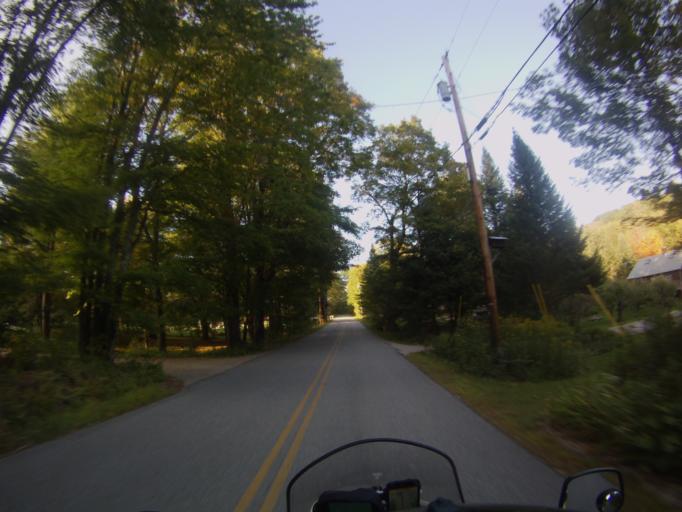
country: US
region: Vermont
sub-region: Addison County
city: Middlebury (village)
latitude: 43.9897
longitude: -73.0335
